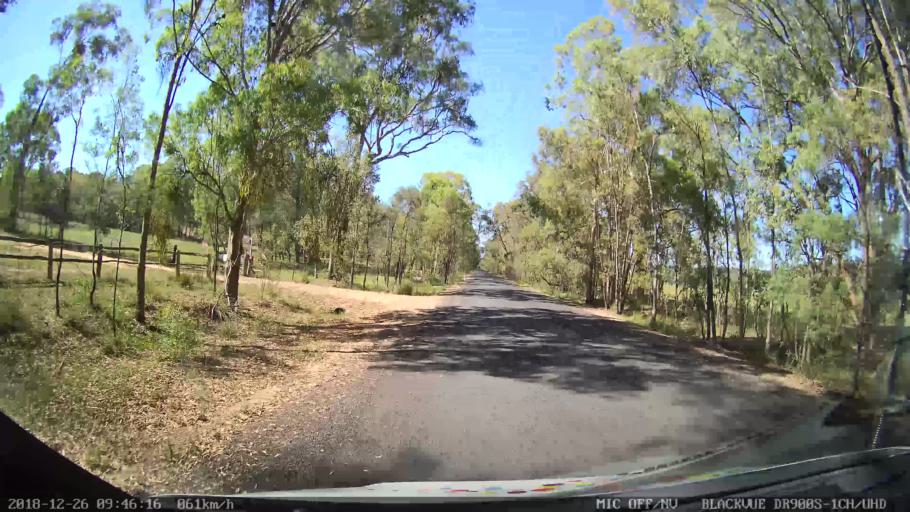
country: AU
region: New South Wales
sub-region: Mid-Western Regional
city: Kandos
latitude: -32.9682
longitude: 150.1056
